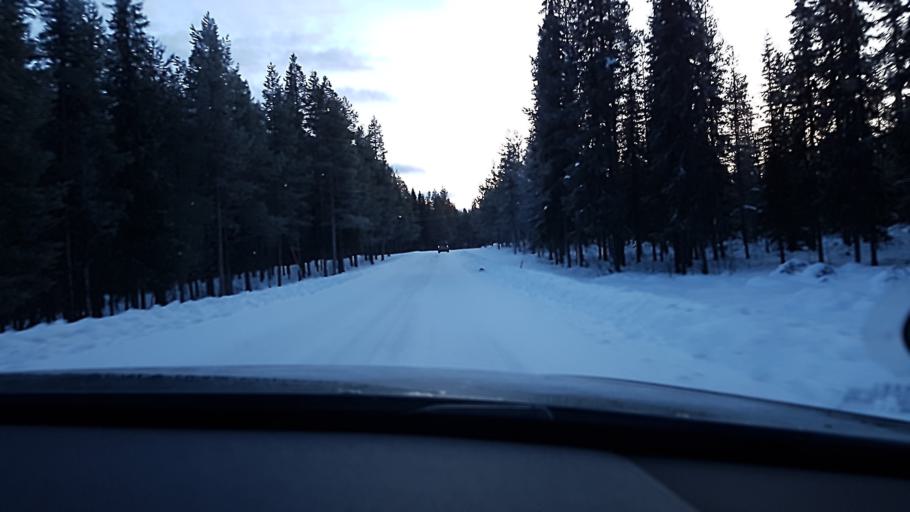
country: SE
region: Vaesterbotten
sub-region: Sorsele Kommun
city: Sorsele
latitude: 65.4990
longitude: 17.5564
